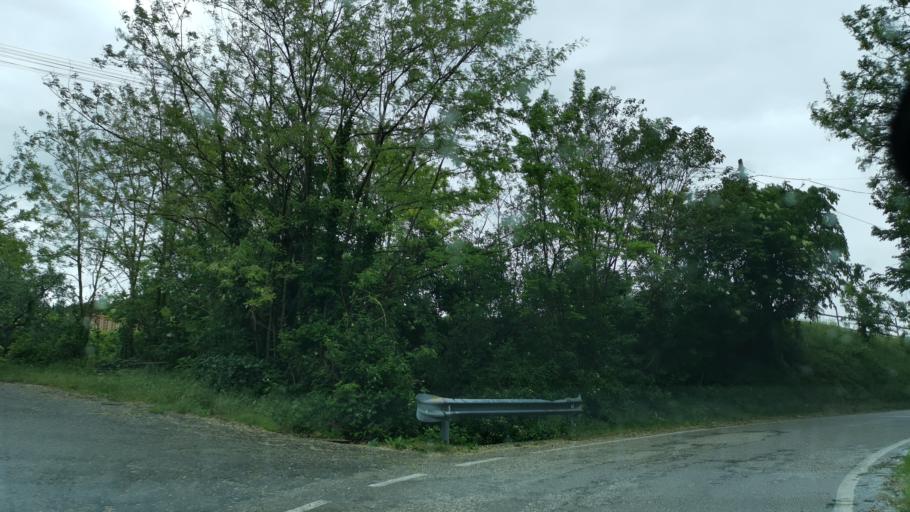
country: IT
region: Veneto
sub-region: Provincia di Verona
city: Cavajon Veronese
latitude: 45.5387
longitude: 10.7529
